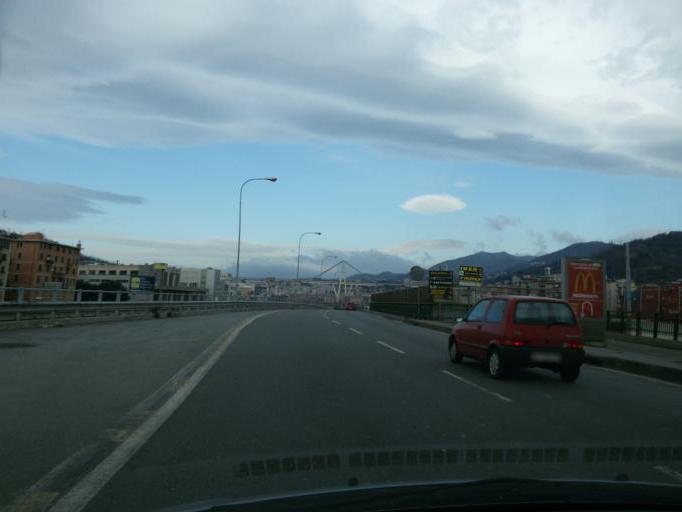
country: IT
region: Liguria
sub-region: Provincia di Genova
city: San Teodoro
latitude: 44.4168
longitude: 8.8816
